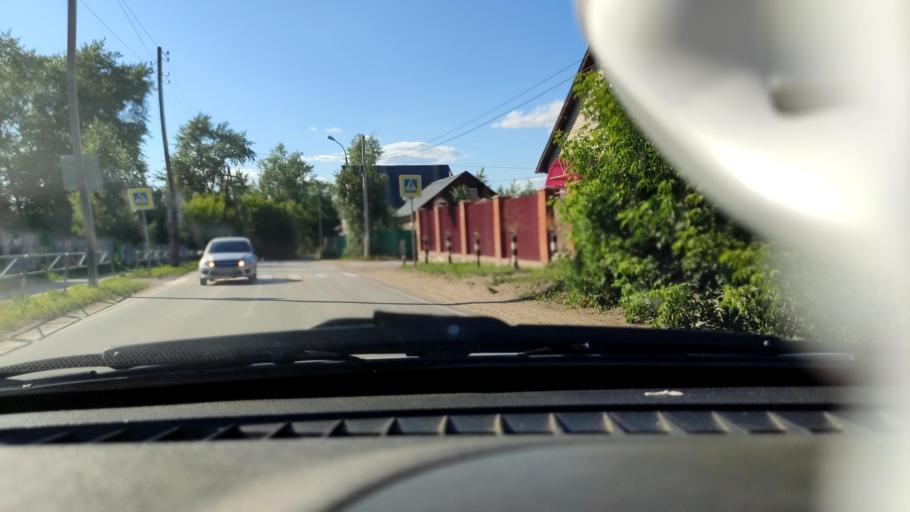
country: RU
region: Perm
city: Krasnokamsk
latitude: 58.0718
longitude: 55.8013
